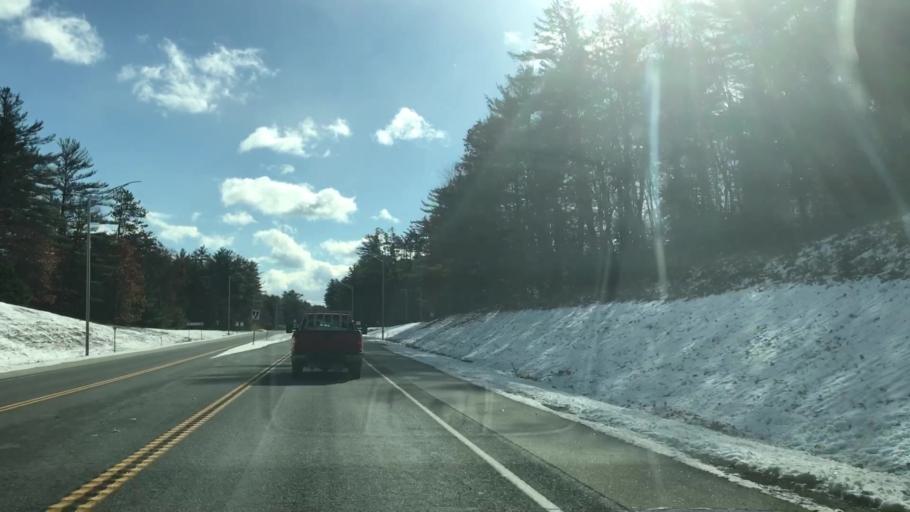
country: US
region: New Hampshire
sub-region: Carroll County
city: Ossipee
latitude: 43.7508
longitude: -71.1349
